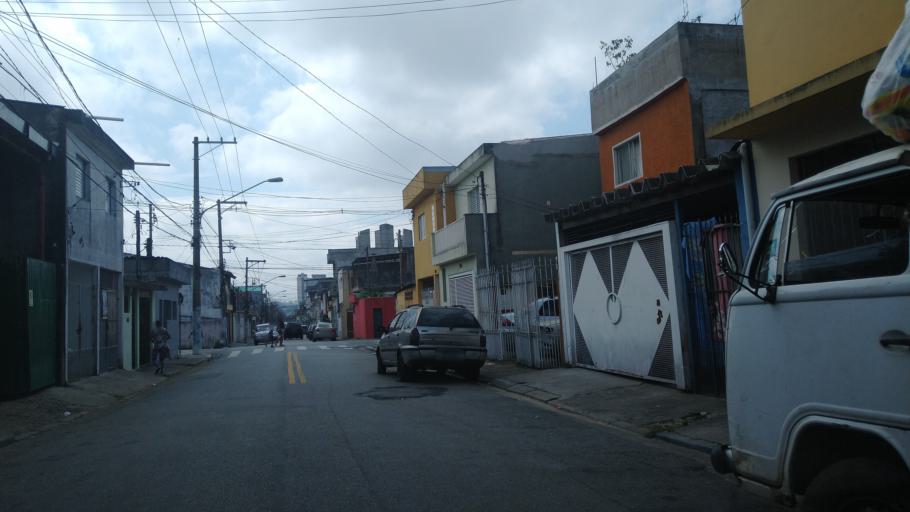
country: BR
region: Sao Paulo
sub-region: Guarulhos
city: Guarulhos
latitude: -23.4873
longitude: -46.5757
